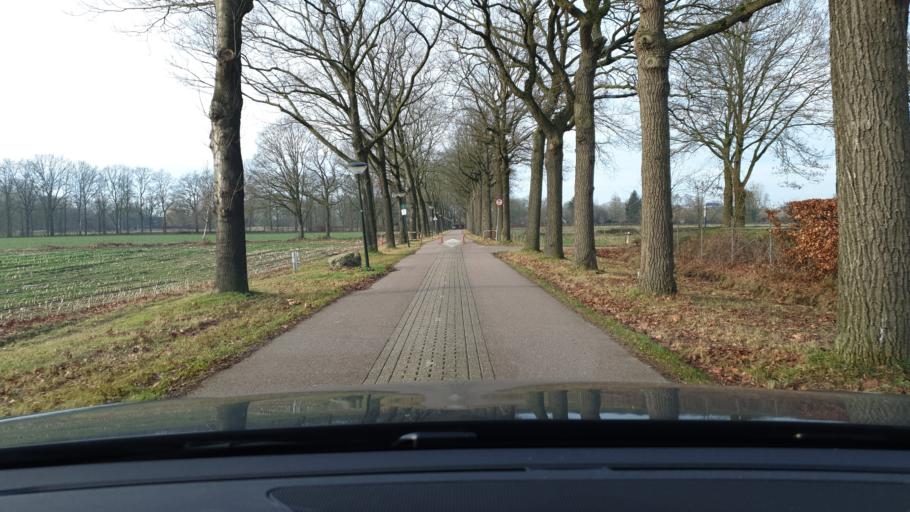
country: NL
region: North Brabant
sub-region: Gemeente Eindhoven
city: Muschberg en Geestenberg
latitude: 51.4218
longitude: 5.5303
